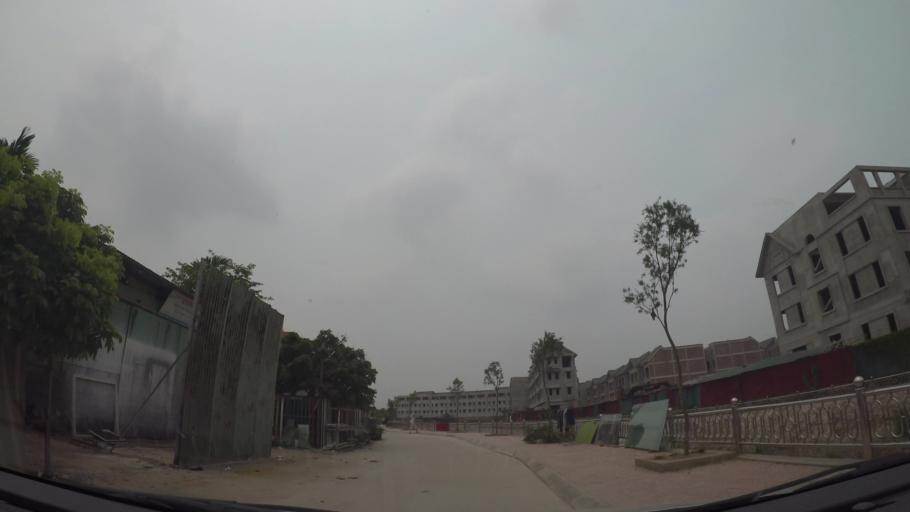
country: VN
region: Ha Noi
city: Ha Dong
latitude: 20.9840
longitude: 105.7484
